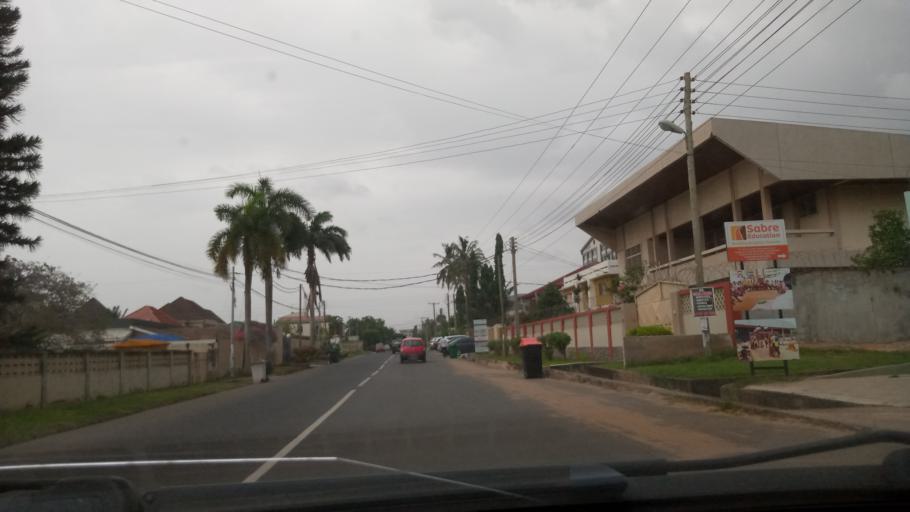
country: GH
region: Greater Accra
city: Dome
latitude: 5.6160
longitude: -0.1976
